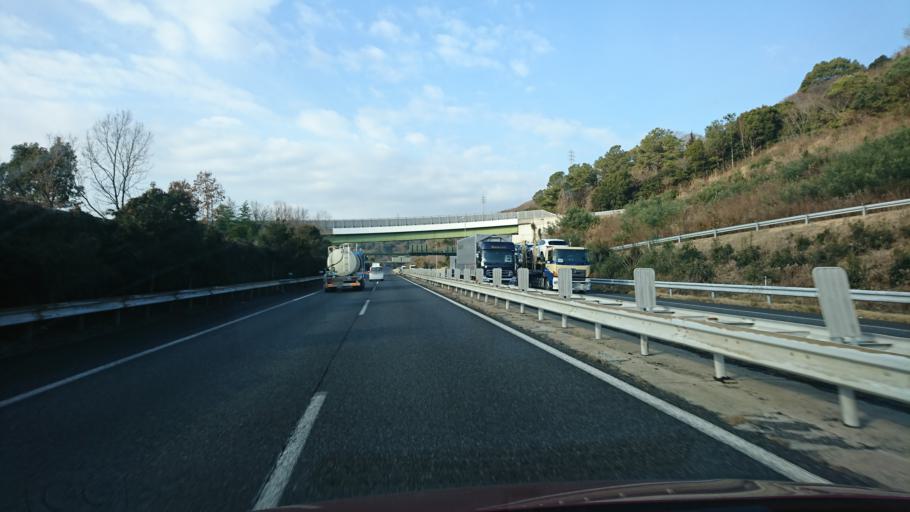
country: JP
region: Hyogo
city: Aioi
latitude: 34.8301
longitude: 134.4903
